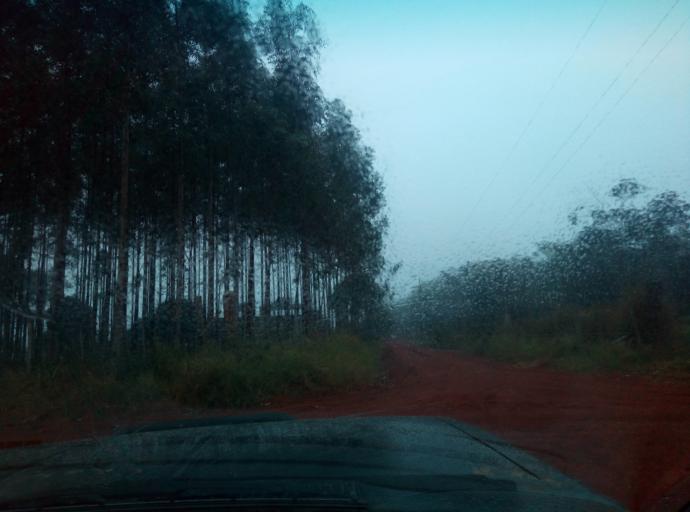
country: PY
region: Caaguazu
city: Doctor Cecilio Baez
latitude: -25.1630
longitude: -56.2621
